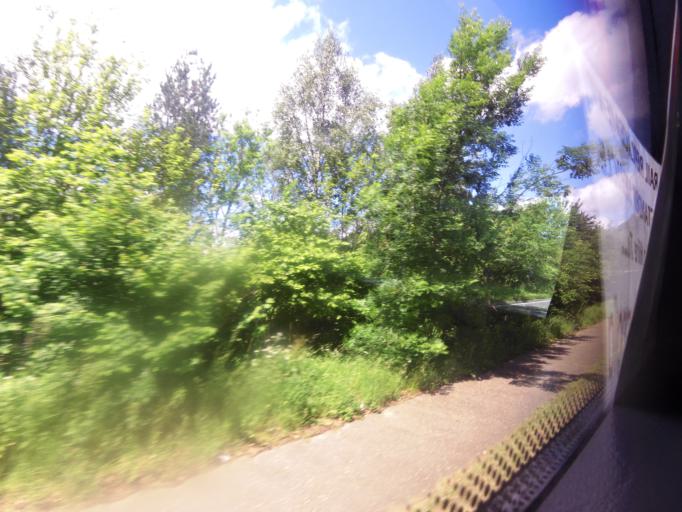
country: GB
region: England
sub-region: Norfolk
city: Aylsham
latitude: 52.7721
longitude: 1.2568
